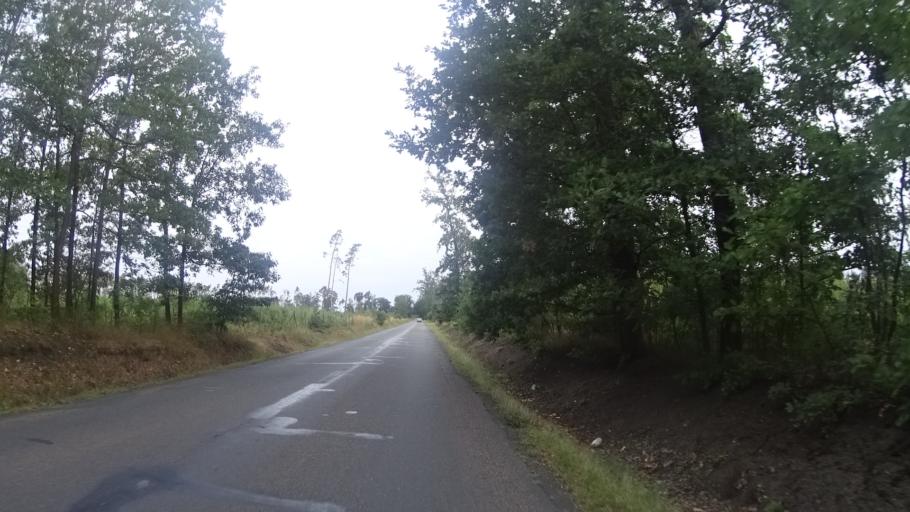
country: CZ
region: Kralovehradecky
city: Cernilov
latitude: 50.2063
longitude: 15.9249
